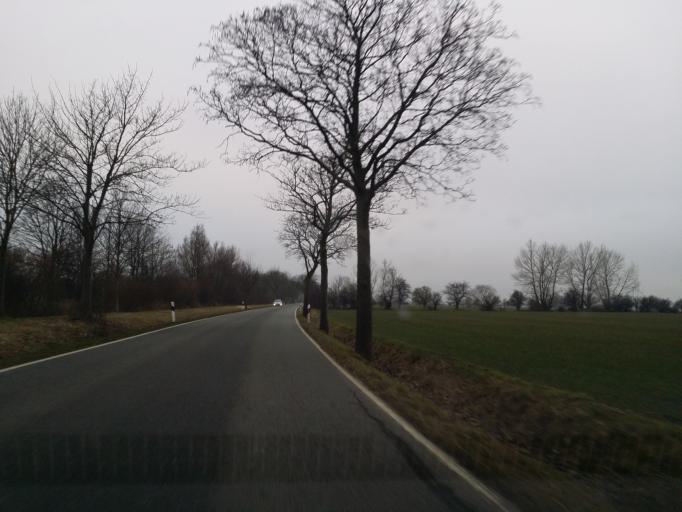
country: DE
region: Schleswig-Holstein
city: Fehmarn
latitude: 54.4596
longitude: 11.1253
